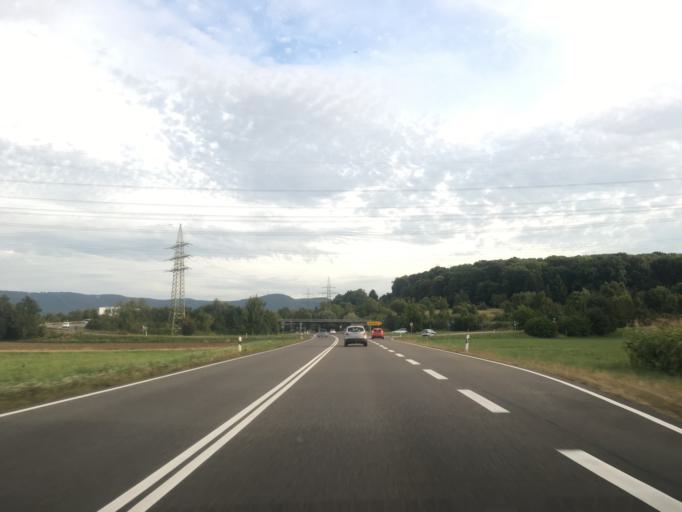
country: DE
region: Baden-Wuerttemberg
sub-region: Tuebingen Region
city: Riederich
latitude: 48.5510
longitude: 9.2625
